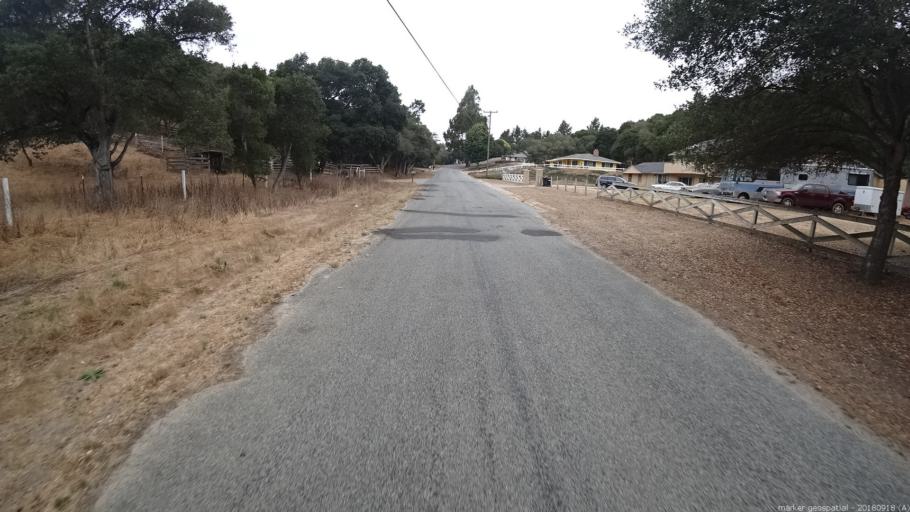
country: US
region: California
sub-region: Monterey County
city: Prunedale
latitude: 36.7848
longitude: -121.6415
